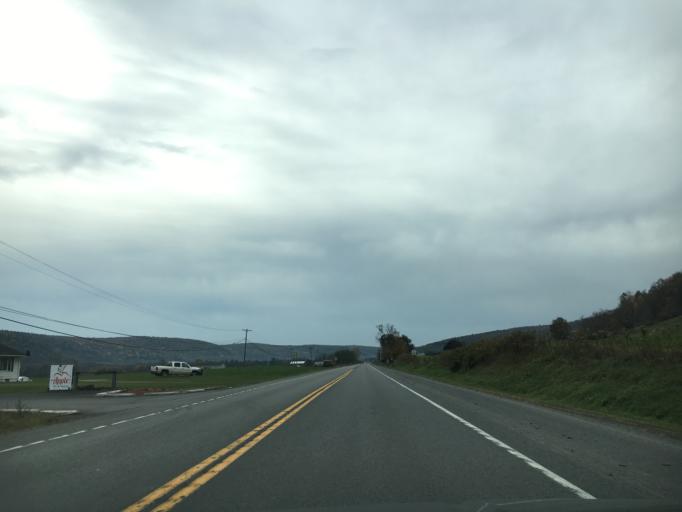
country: US
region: New York
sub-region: Otsego County
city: Cooperstown
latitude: 42.5802
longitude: -74.9486
